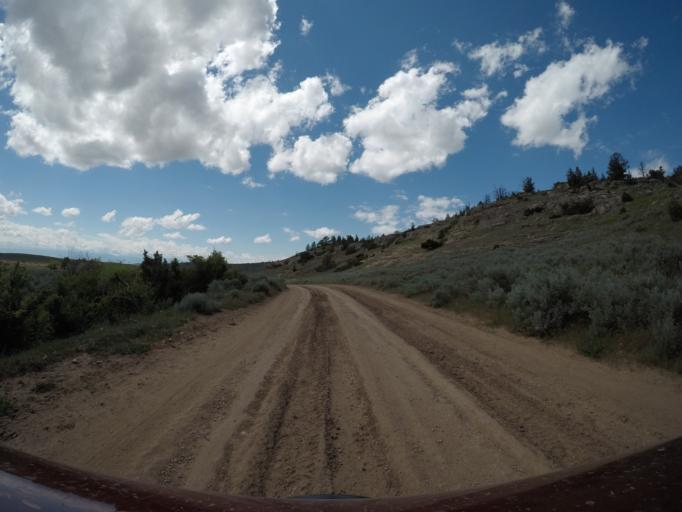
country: US
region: Montana
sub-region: Yellowstone County
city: Laurel
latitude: 45.2439
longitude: -108.6499
